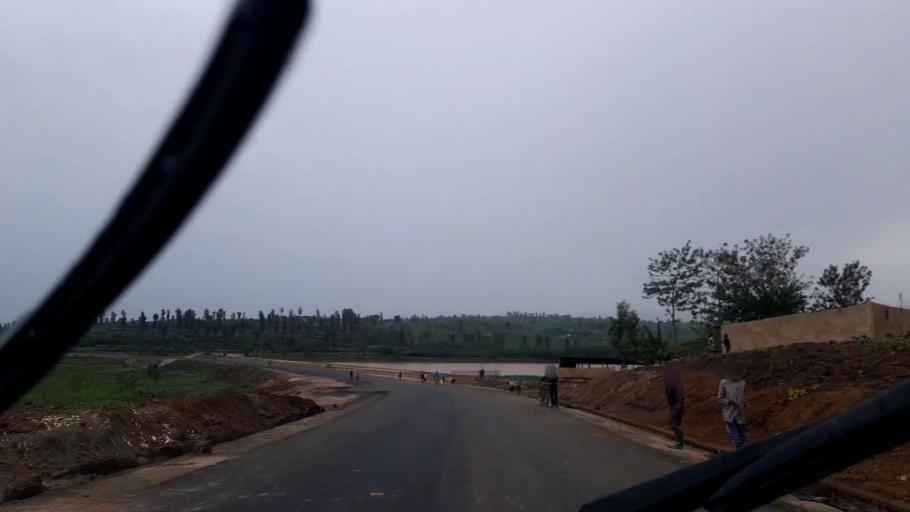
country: RW
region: Northern Province
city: Byumba
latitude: -1.4124
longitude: 30.2835
